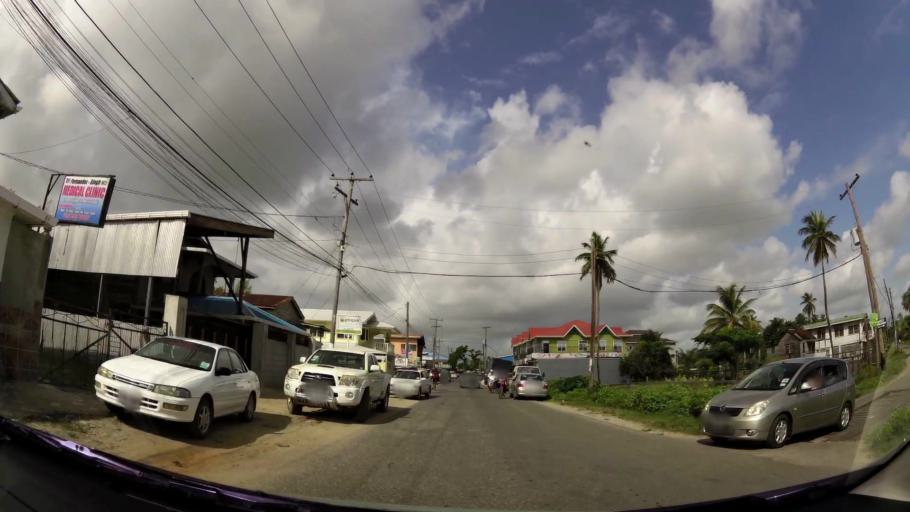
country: GY
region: Demerara-Mahaica
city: Mahaica Village
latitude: 6.6719
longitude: -57.9228
